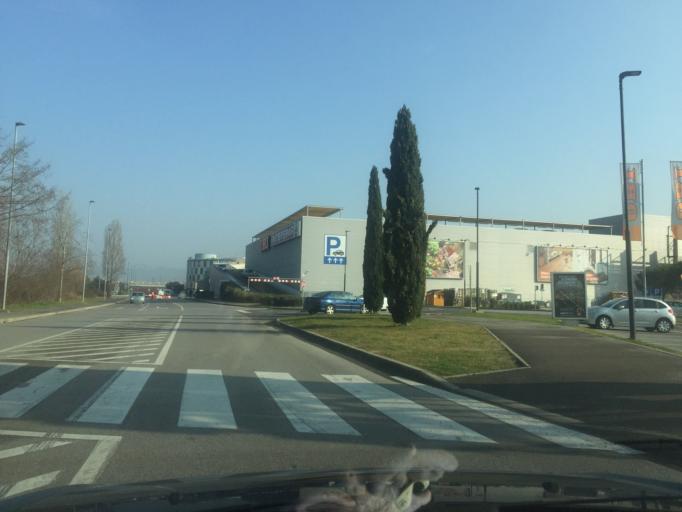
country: SI
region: Koper-Capodistria
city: Koper
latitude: 45.5444
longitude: 13.7385
